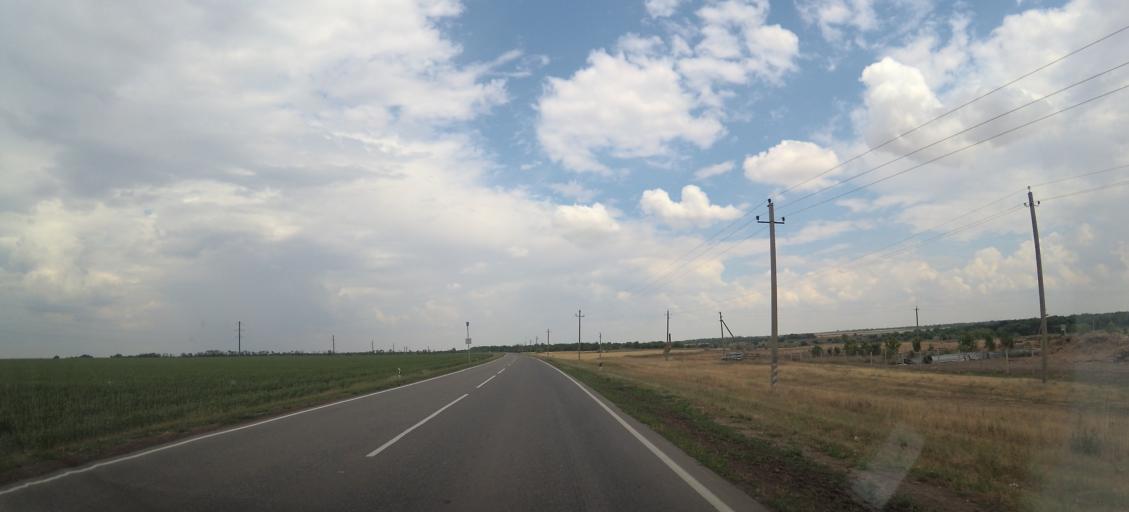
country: RU
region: Rostov
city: Krasnaya Polyana
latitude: 46.2502
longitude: 41.3295
